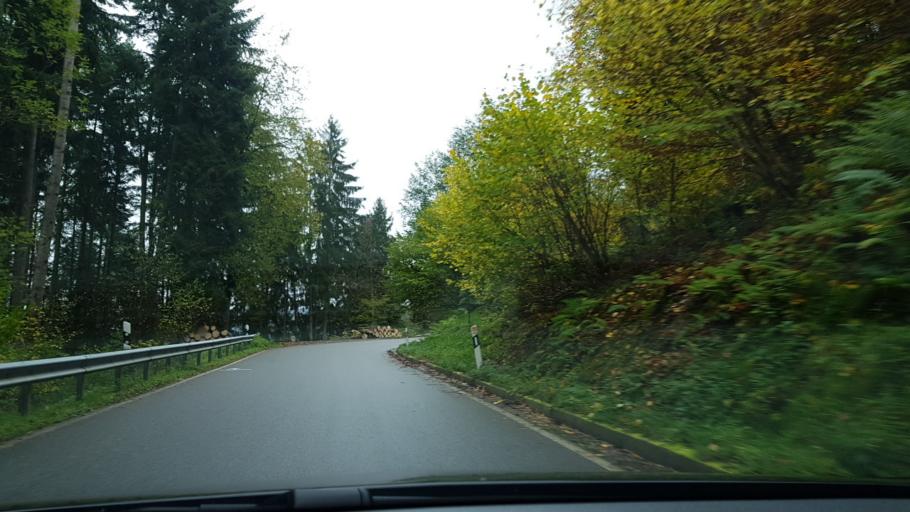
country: DE
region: Rheinland-Pfalz
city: Mehring
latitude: 49.7844
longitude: 6.8365
